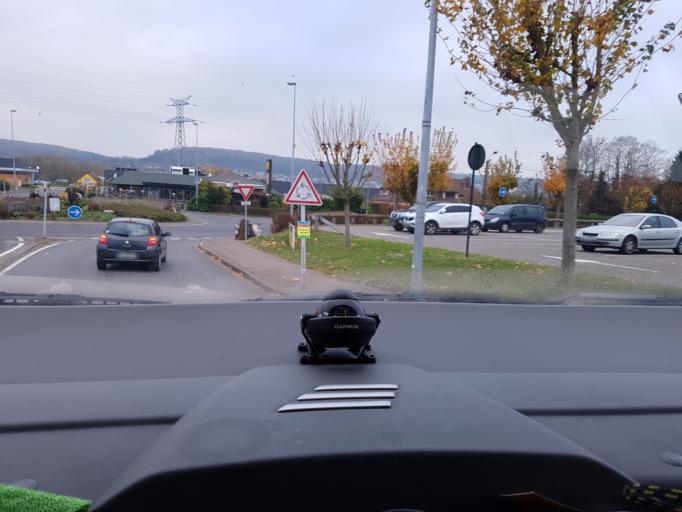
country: FR
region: Picardie
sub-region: Departement de la Somme
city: Mers-les-Bains
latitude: 50.0616
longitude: 1.4075
